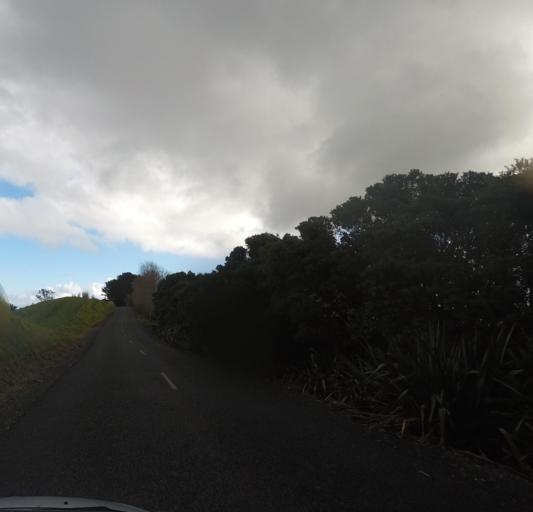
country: NZ
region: Auckland
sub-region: Auckland
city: Warkworth
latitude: -36.3725
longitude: 174.7640
